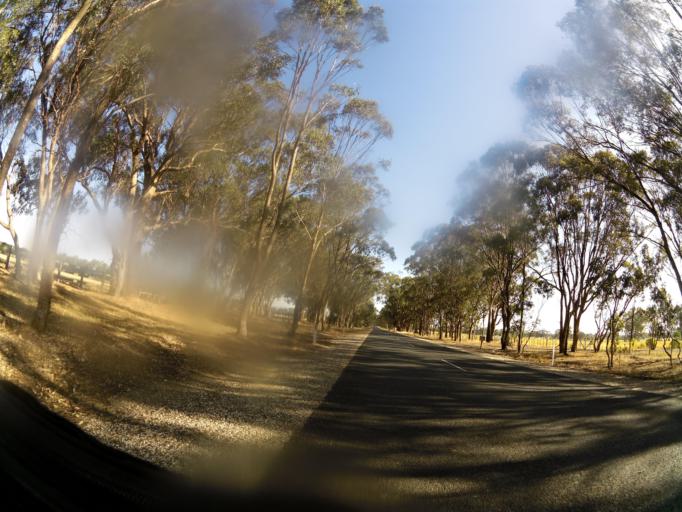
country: AU
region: Victoria
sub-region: Murrindindi
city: Kinglake West
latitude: -36.9664
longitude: 145.1087
